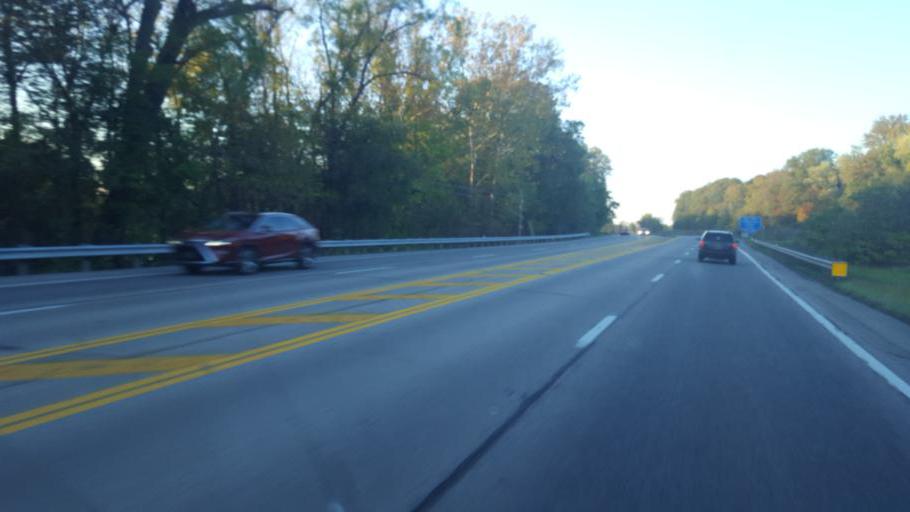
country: US
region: Ohio
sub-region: Scioto County
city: Lucasville
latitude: 38.9360
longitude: -83.0222
